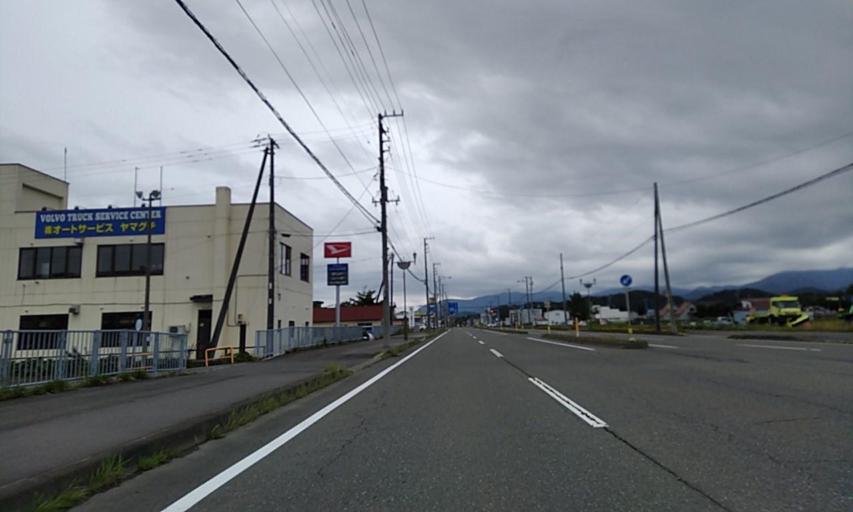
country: JP
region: Hokkaido
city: Obihiro
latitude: 42.3050
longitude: 143.3180
